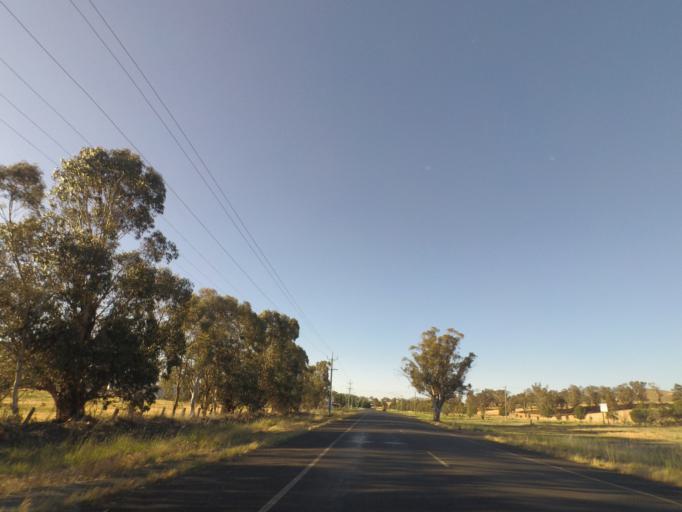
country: AU
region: New South Wales
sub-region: Gundagai
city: Gundagai
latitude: -34.9304
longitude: 148.1665
